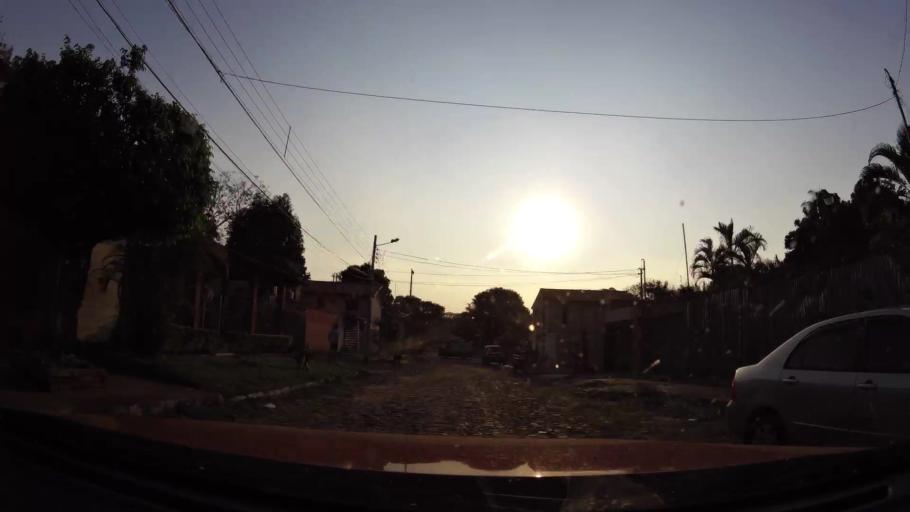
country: PY
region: Central
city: Lambare
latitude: -25.3451
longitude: -57.6048
